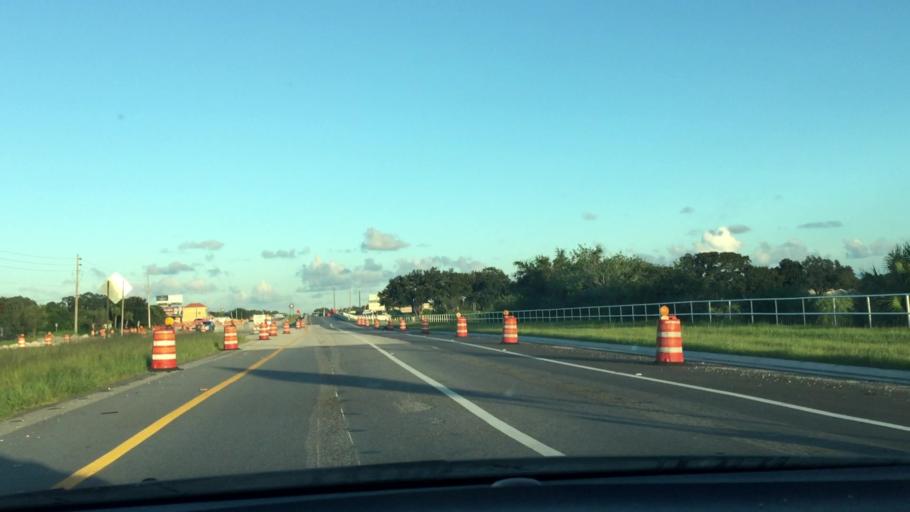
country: US
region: Florida
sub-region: Osceola County
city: Saint Cloud
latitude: 28.2592
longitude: -81.3252
